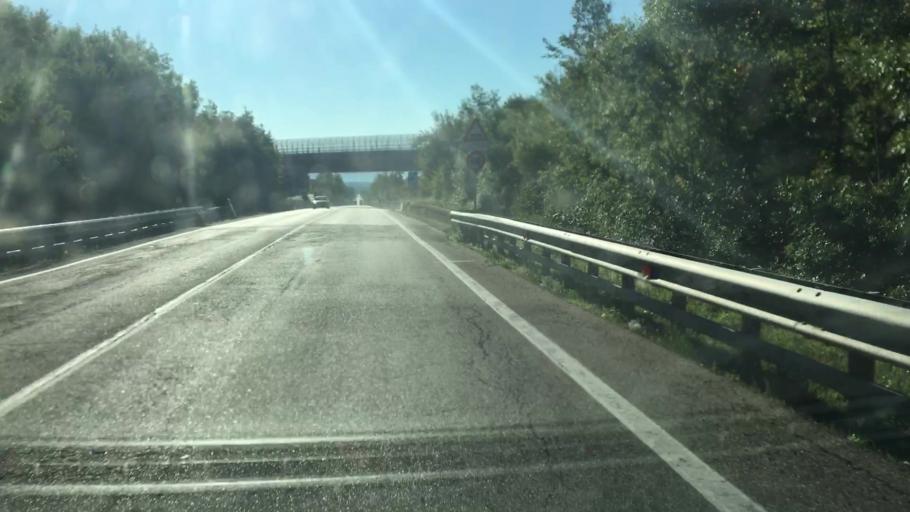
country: IT
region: Molise
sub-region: Provincia di Campobasso
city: Vinchiaturo
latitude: 41.4528
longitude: 14.5854
